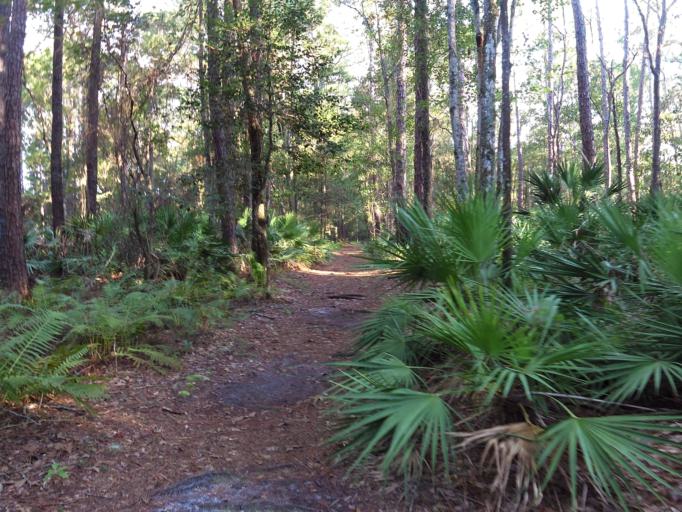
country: US
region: Florida
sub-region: Clay County
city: Orange Park
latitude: 30.2433
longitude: -81.6979
